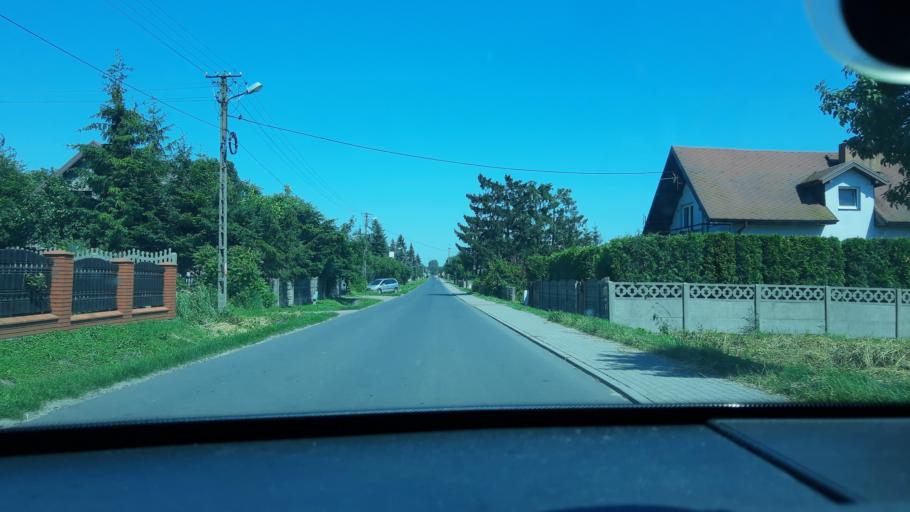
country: PL
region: Lodz Voivodeship
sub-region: Powiat zdunskowolski
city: Zdunska Wola
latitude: 51.6206
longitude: 18.9468
